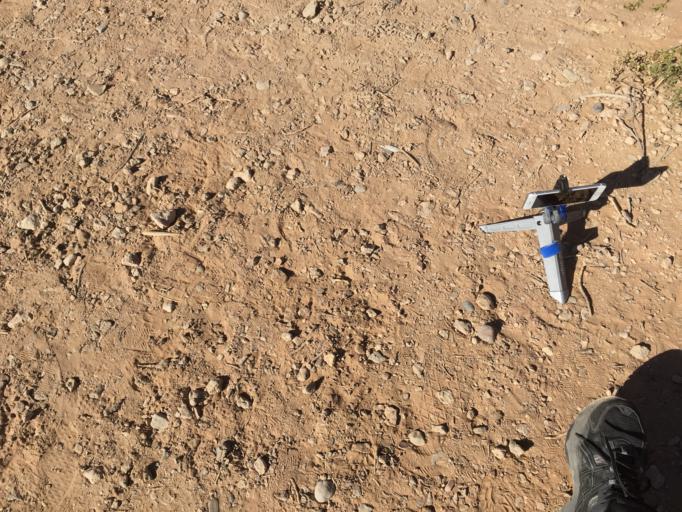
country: US
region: Nevada
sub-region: Clark County
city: Enterprise
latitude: 35.8381
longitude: -115.2712
